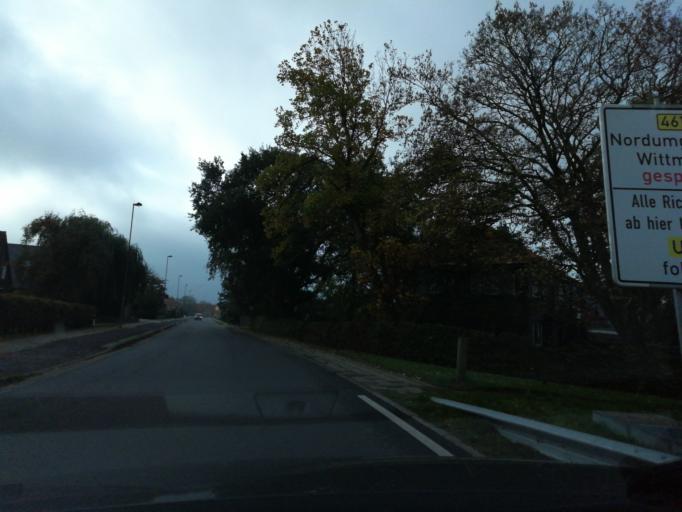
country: DE
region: Lower Saxony
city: Werdum
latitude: 53.6940
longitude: 7.8063
